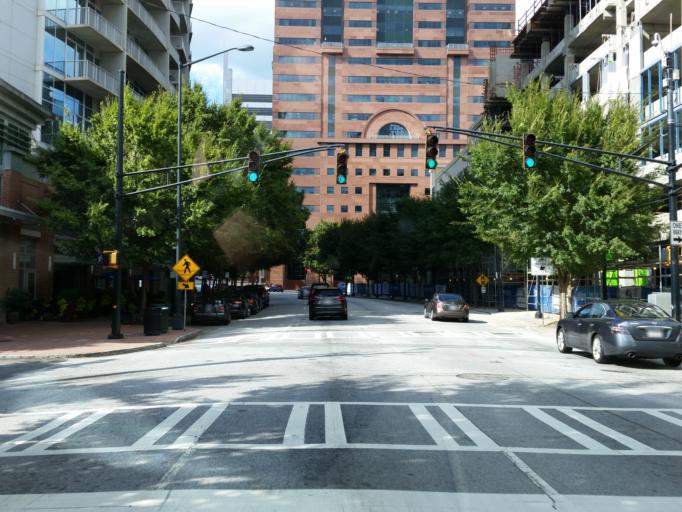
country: US
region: Georgia
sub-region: Fulton County
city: Atlanta
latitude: 33.7798
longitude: -84.3874
